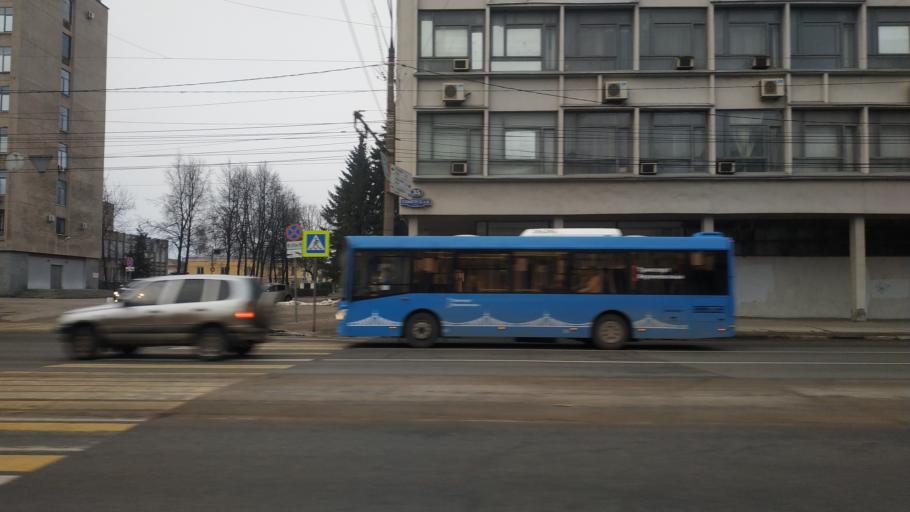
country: RU
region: Tverskaya
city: Tver
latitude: 56.8579
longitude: 35.9232
